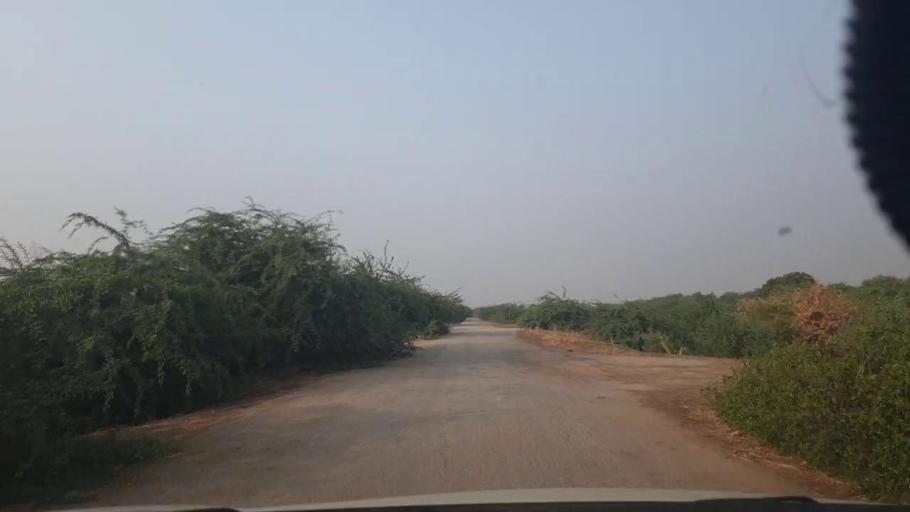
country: PK
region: Sindh
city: Bulri
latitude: 24.8301
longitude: 68.4029
